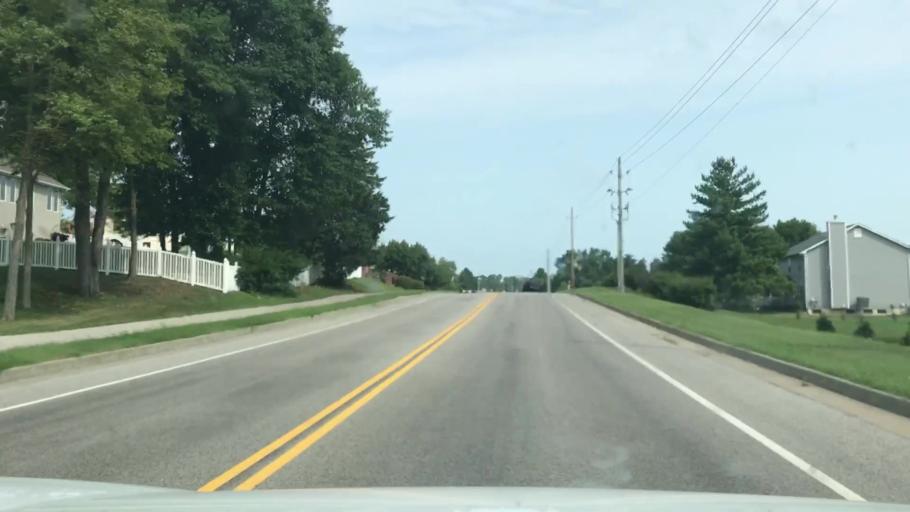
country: US
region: Missouri
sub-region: Saint Charles County
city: Cottleville
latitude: 38.7223
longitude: -90.6427
